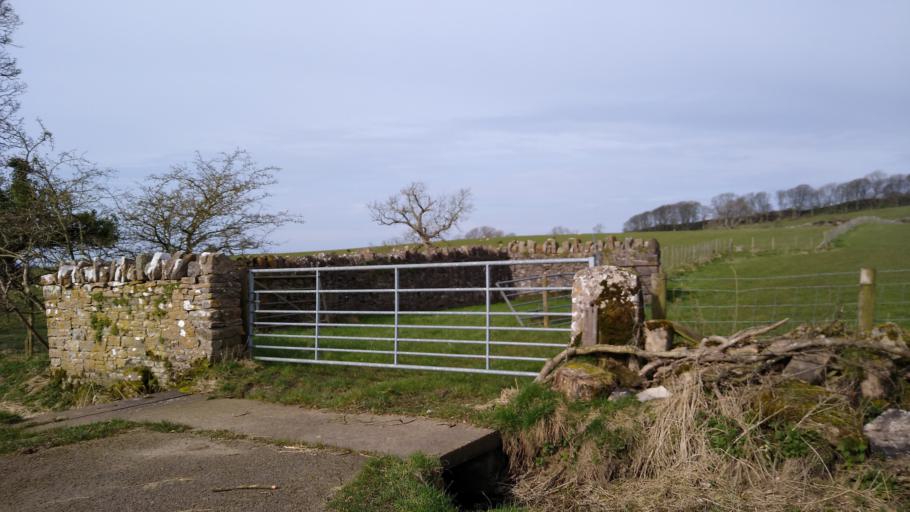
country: GB
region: England
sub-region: Cumbria
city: Cockermouth
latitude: 54.6937
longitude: -3.3681
